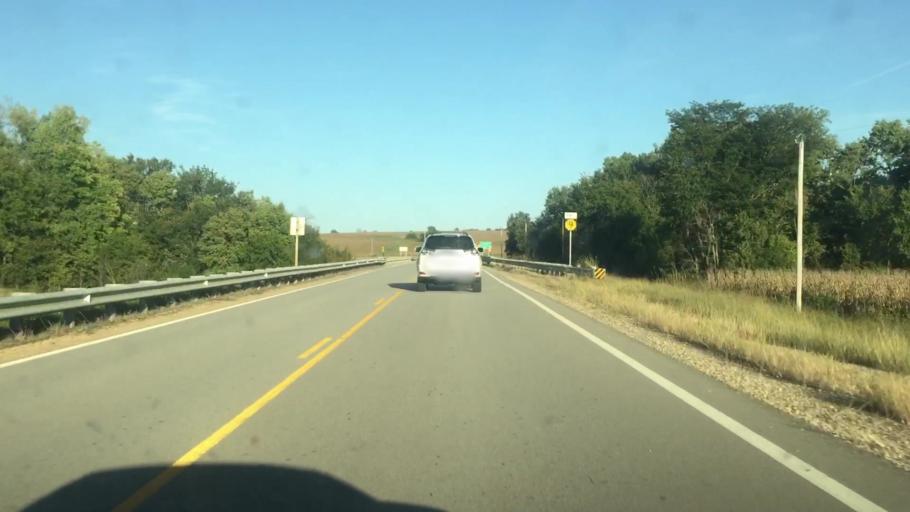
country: US
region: Kansas
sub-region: Brown County
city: Horton
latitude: 39.5874
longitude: -95.5316
